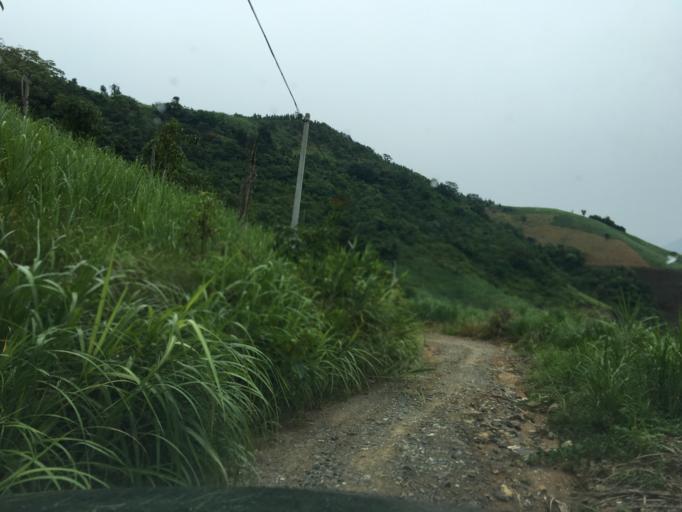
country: CN
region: Guangxi Zhuangzu Zizhiqu
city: Tongle
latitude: 25.0043
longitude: 105.9862
